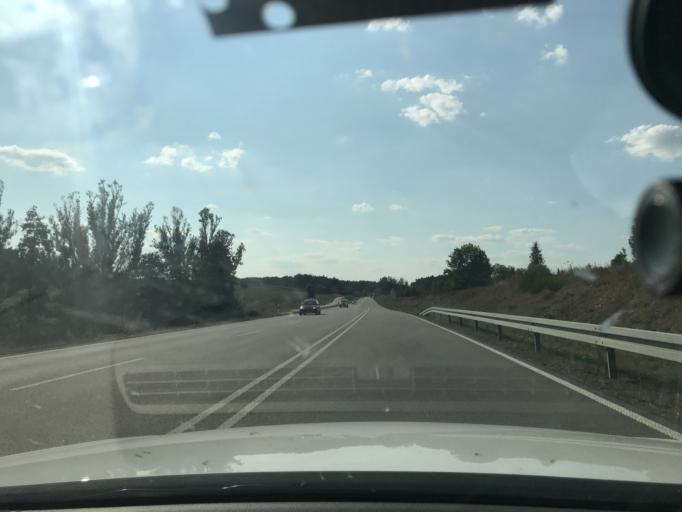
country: DE
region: Bavaria
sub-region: Upper Palatinate
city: Poppenricht
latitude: 49.4621
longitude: 11.7973
